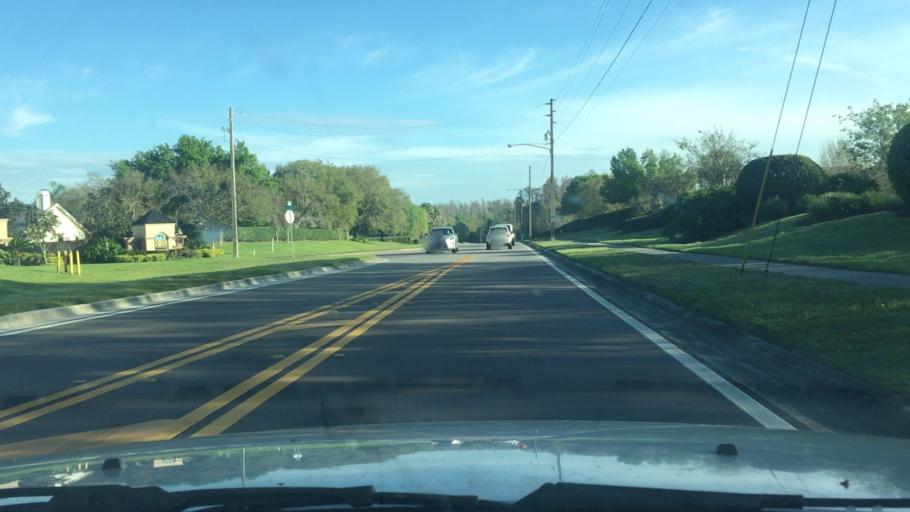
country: US
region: Florida
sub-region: Pasco County
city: Land O' Lakes
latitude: 28.2167
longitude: -82.4372
